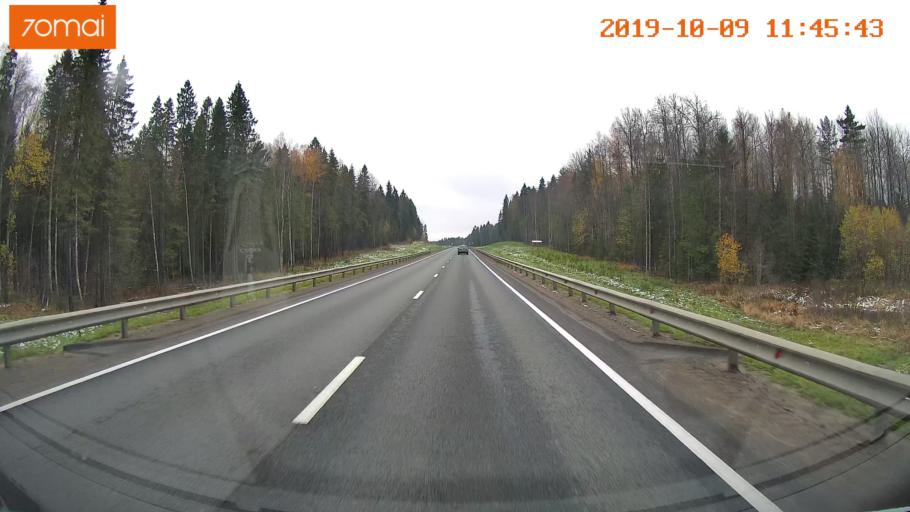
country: RU
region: Vologda
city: Gryazovets
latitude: 58.8646
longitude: 40.1981
